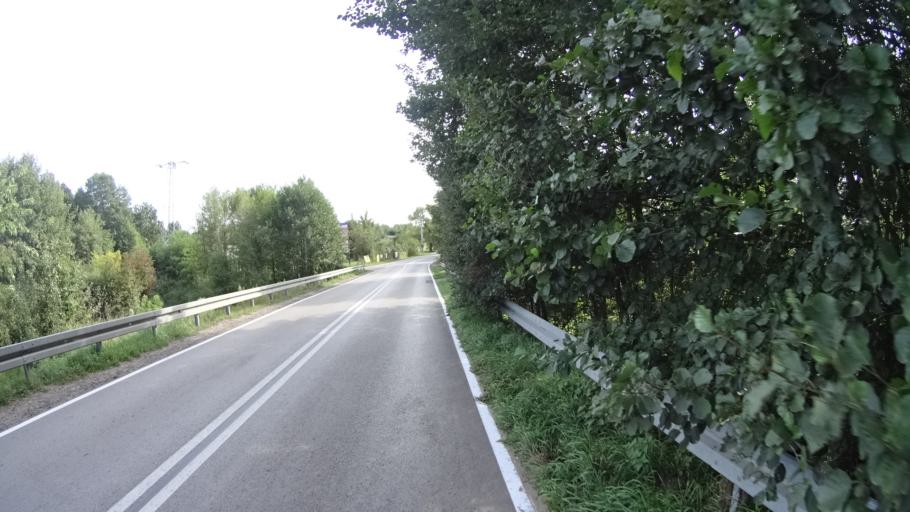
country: PL
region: Masovian Voivodeship
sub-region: Powiat legionowski
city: Serock
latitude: 52.4766
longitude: 21.0926
